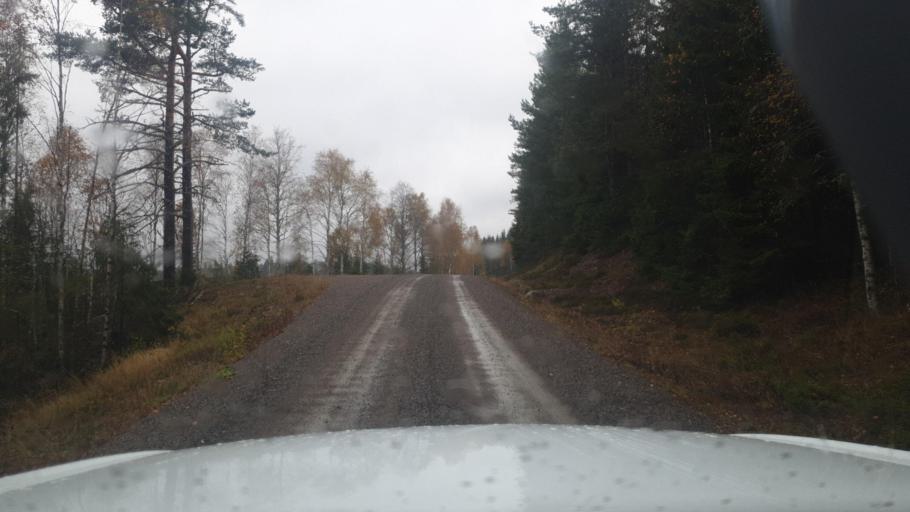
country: SE
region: Vaermland
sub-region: Eda Kommun
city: Charlottenberg
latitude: 60.1042
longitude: 12.6067
